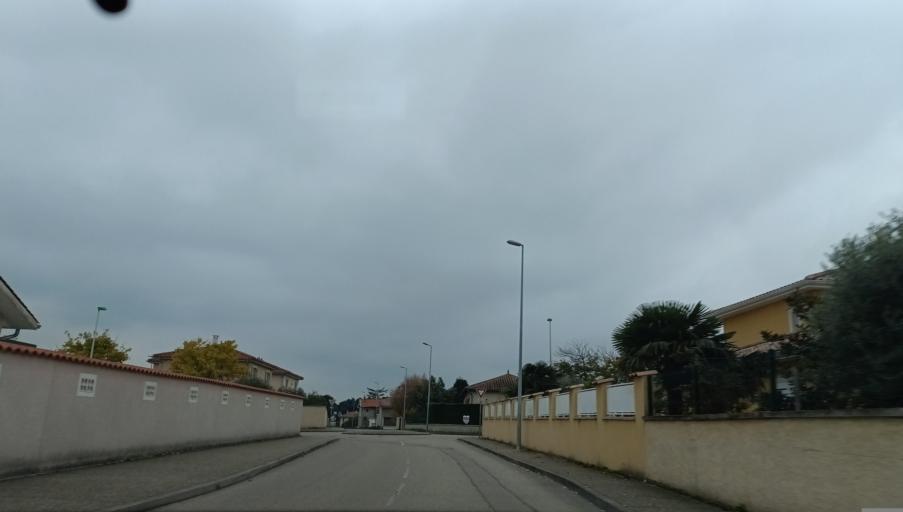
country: FR
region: Rhone-Alpes
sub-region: Departement de l'Isere
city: Chasse-sur-Rhone
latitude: 45.5775
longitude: 4.8274
